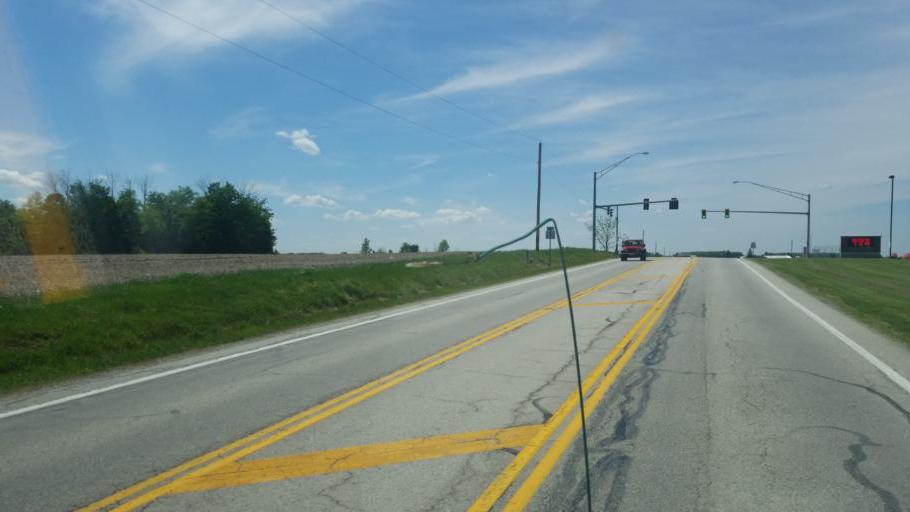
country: US
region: Ohio
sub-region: Huron County
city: Willard
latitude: 41.0765
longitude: -82.9174
